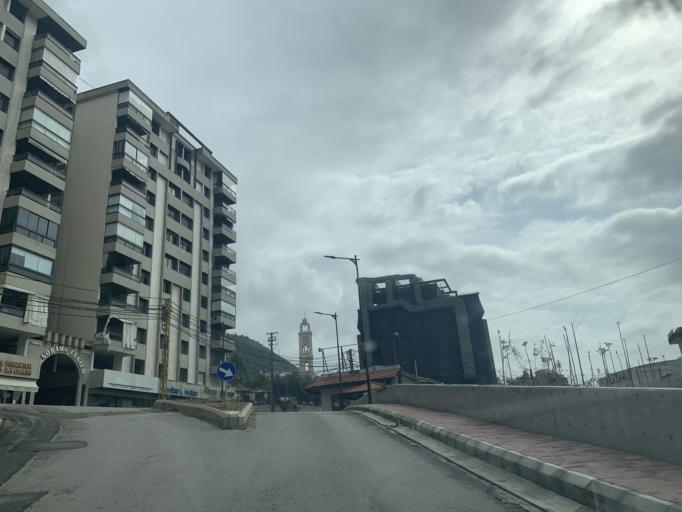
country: LB
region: Mont-Liban
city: Djounie
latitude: 33.9889
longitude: 35.6444
